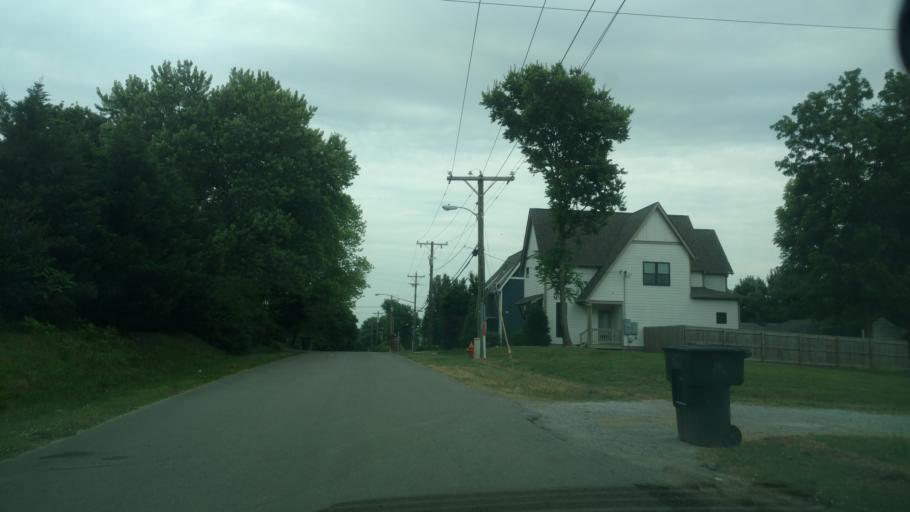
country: US
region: Tennessee
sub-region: Davidson County
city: Nashville
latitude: 36.1915
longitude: -86.7201
